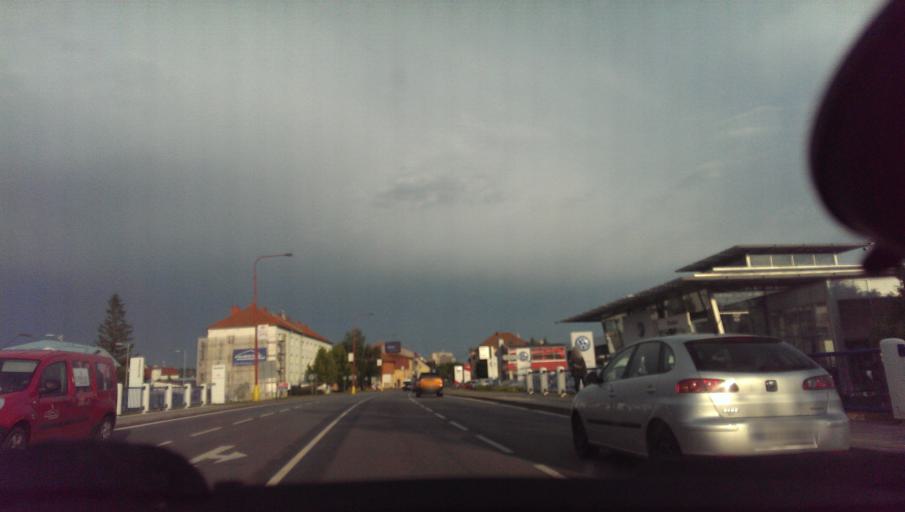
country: CZ
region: Zlin
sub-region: Okres Uherske Hradiste
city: Uherske Hradiste
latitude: 49.0751
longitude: 17.4556
